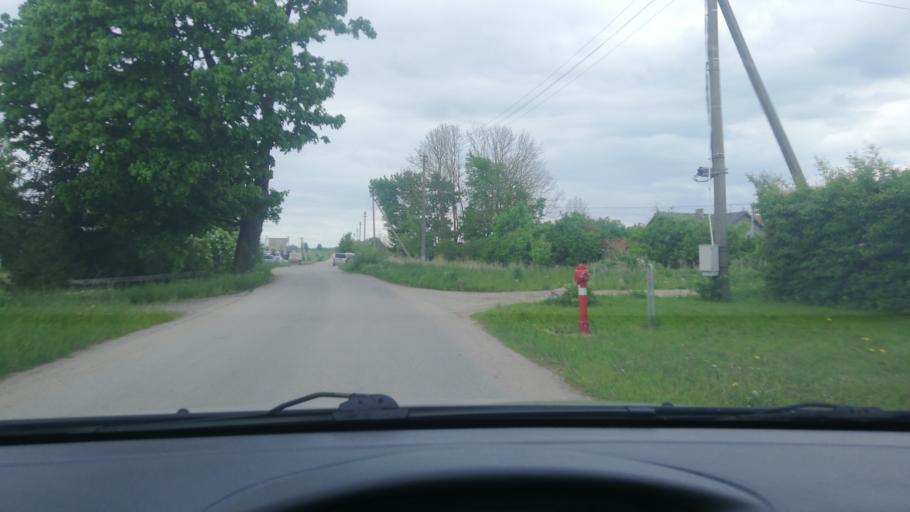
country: LT
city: Priekule
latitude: 55.6456
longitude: 21.2978
